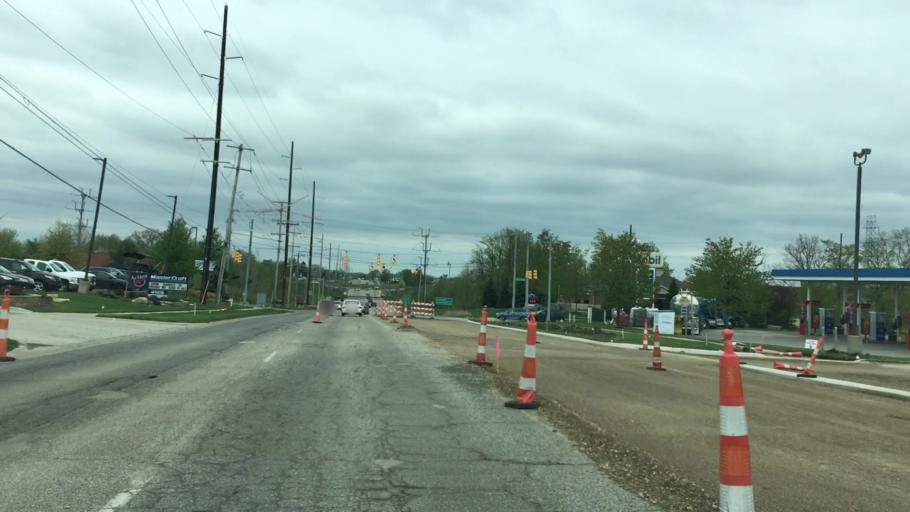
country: US
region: Michigan
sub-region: Ottawa County
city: Hudsonville
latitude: 42.8441
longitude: -85.8617
